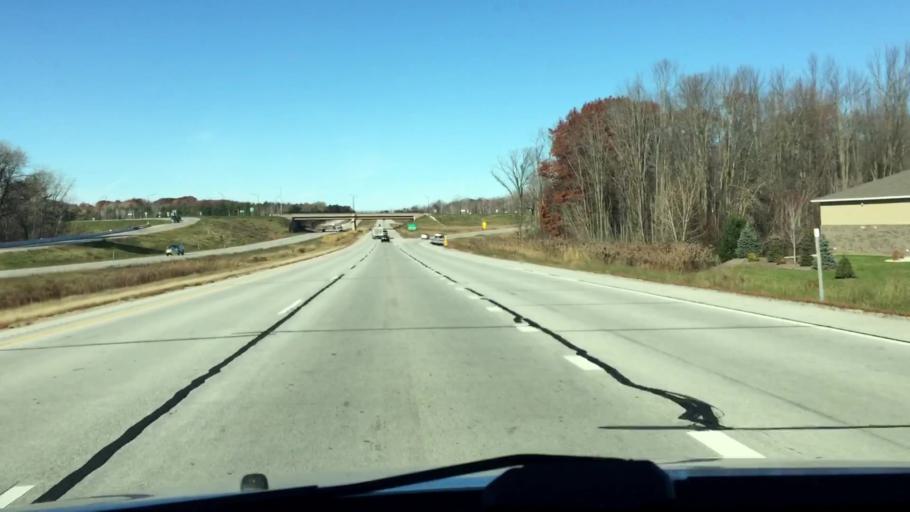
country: US
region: Wisconsin
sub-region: Brown County
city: Howard
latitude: 44.5585
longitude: -88.1252
